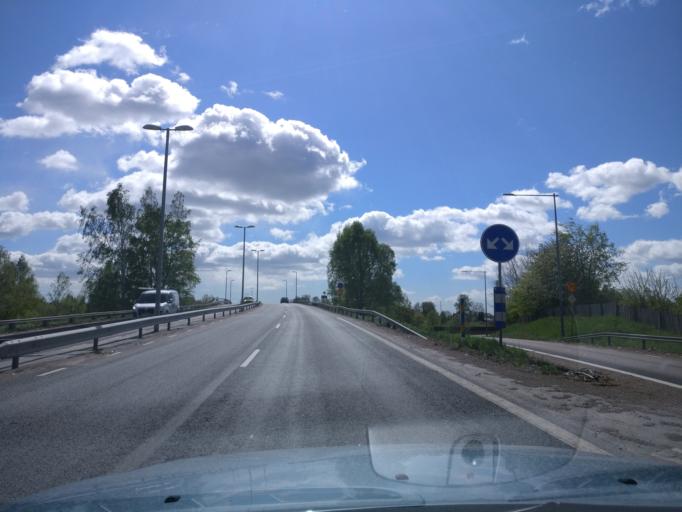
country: SE
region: Vaermland
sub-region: Karlstads Kommun
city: Karlstad
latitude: 59.3898
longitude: 13.5321
